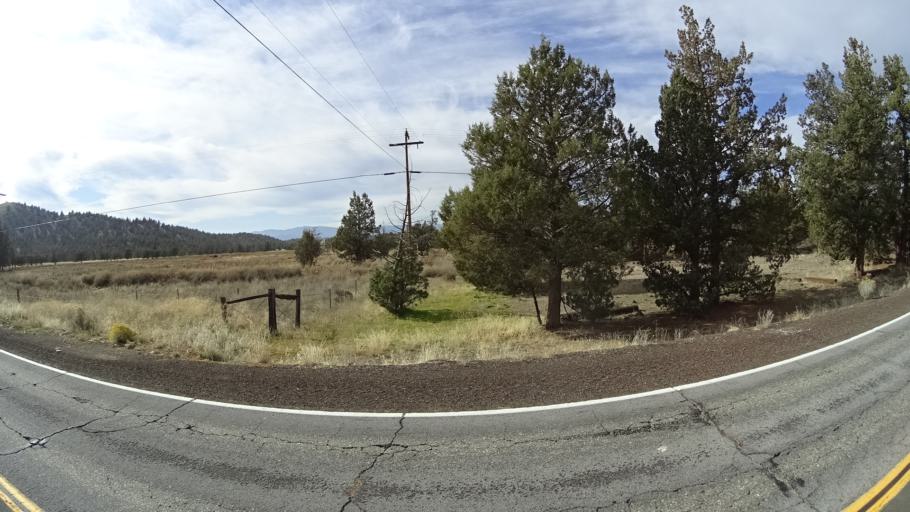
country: US
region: California
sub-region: Siskiyou County
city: Weed
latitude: 41.5827
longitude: -122.3996
